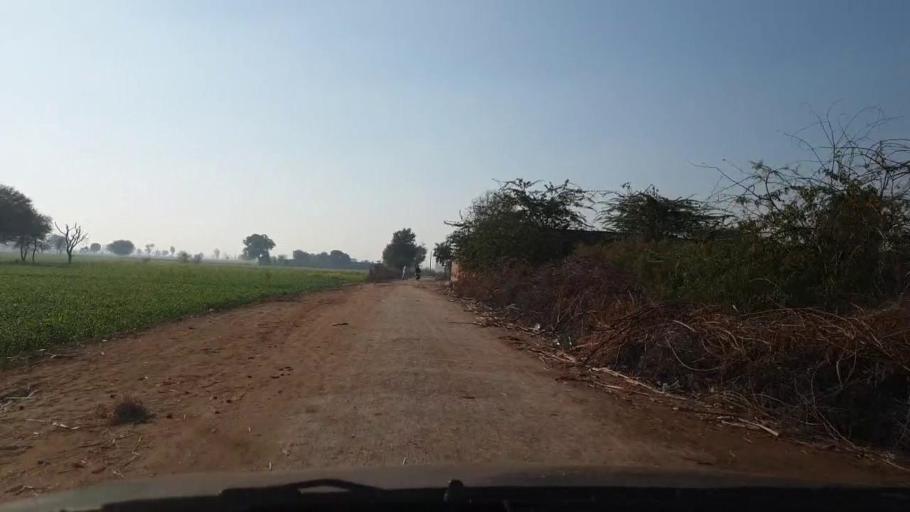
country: PK
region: Sindh
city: Jhol
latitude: 25.9326
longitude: 68.8654
